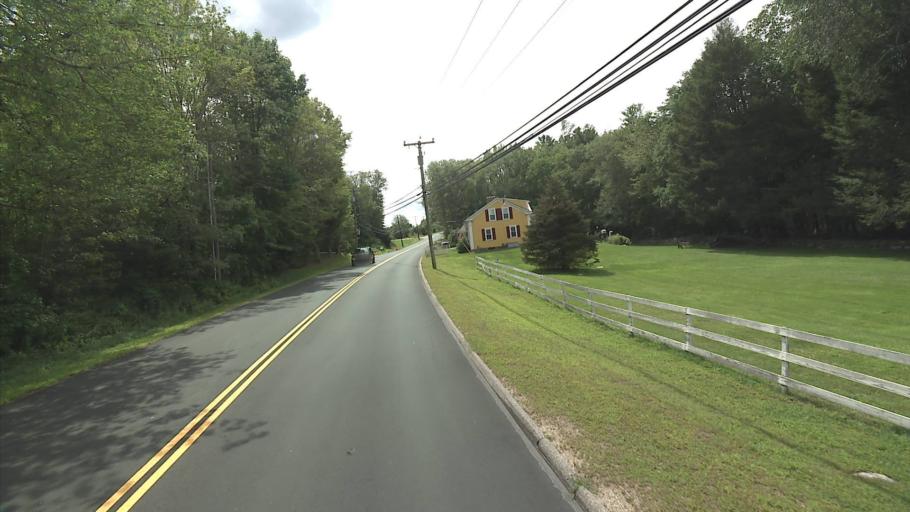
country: US
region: Connecticut
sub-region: Windham County
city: South Woodstock
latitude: 41.9346
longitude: -72.0766
